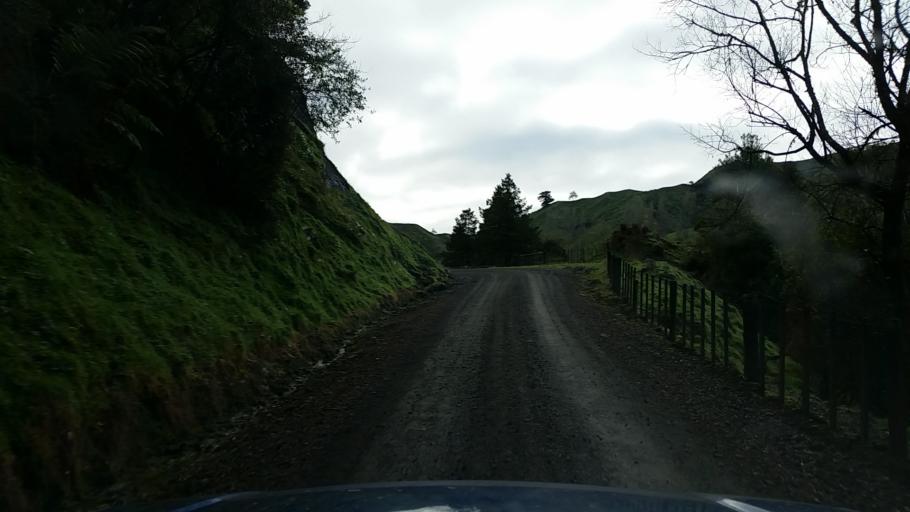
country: NZ
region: Taranaki
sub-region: New Plymouth District
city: Waitara
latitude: -39.0976
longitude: 174.8385
